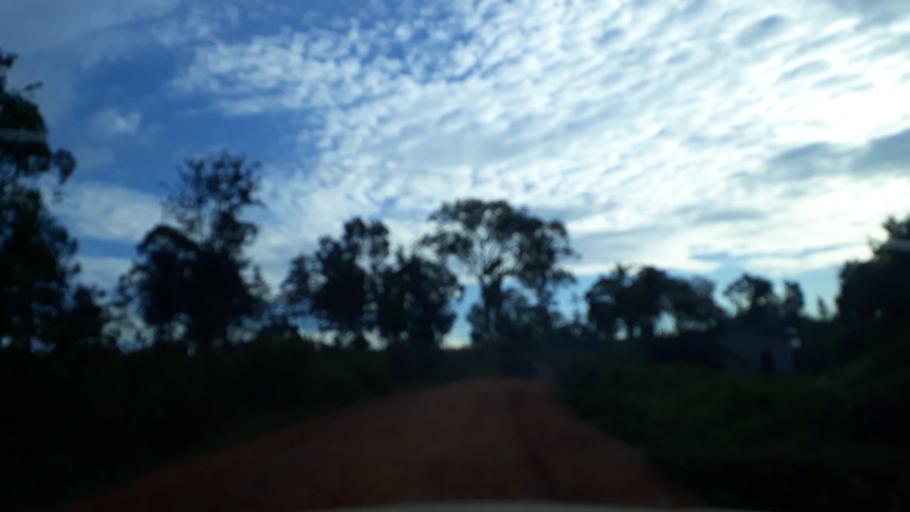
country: UG
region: Northern Region
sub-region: Zombo District
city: Paidha
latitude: 2.2325
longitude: 30.8263
